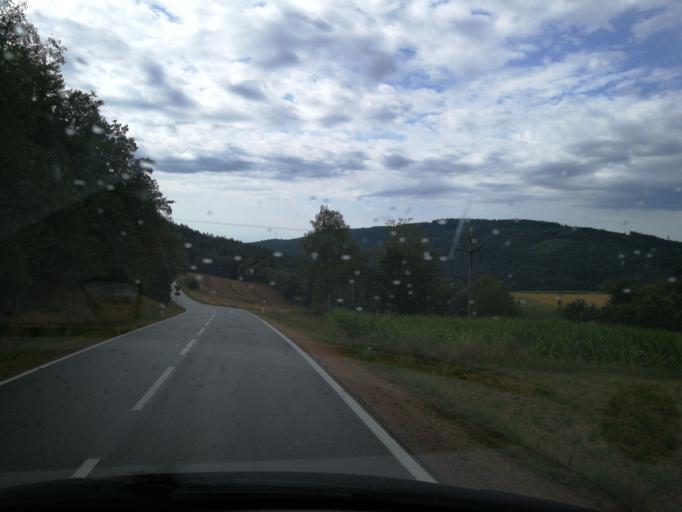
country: DE
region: Bavaria
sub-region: Upper Palatinate
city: Brennberg
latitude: 49.0794
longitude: 12.3548
